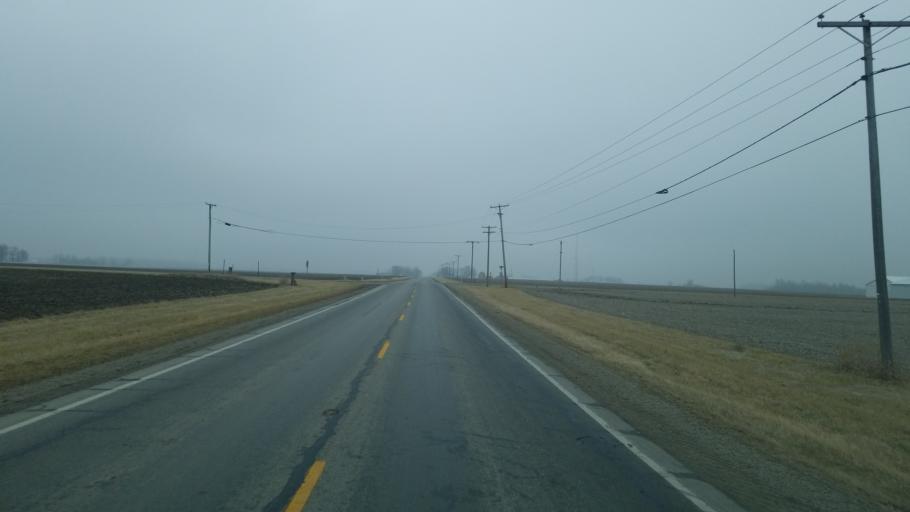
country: US
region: Indiana
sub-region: Adams County
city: Decatur
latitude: 40.7453
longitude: -84.9199
